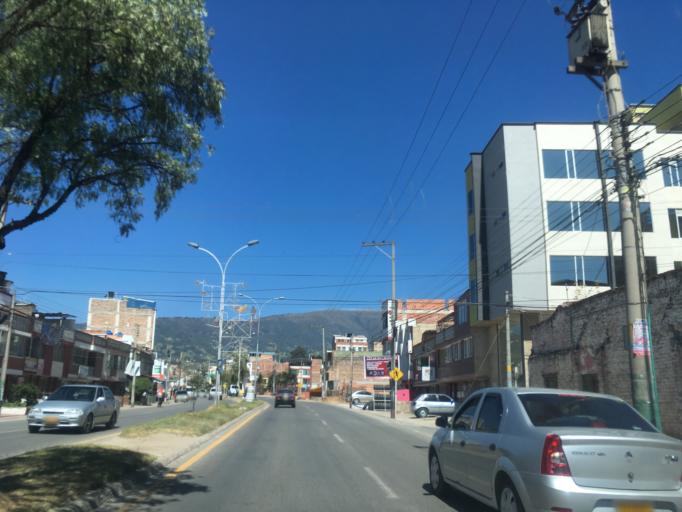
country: CO
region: Boyaca
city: Duitama
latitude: 5.8217
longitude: -73.0255
